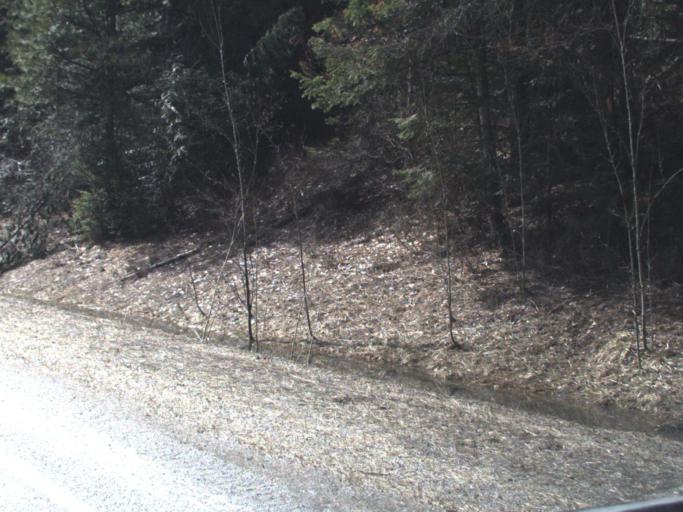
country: US
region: Washington
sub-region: Pend Oreille County
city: Newport
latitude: 48.4191
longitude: -117.3191
